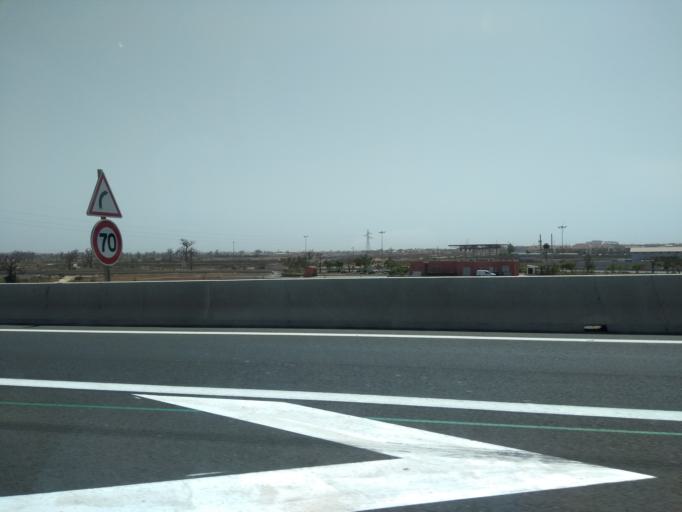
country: SN
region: Thies
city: Pout
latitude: 14.7303
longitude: -17.1583
